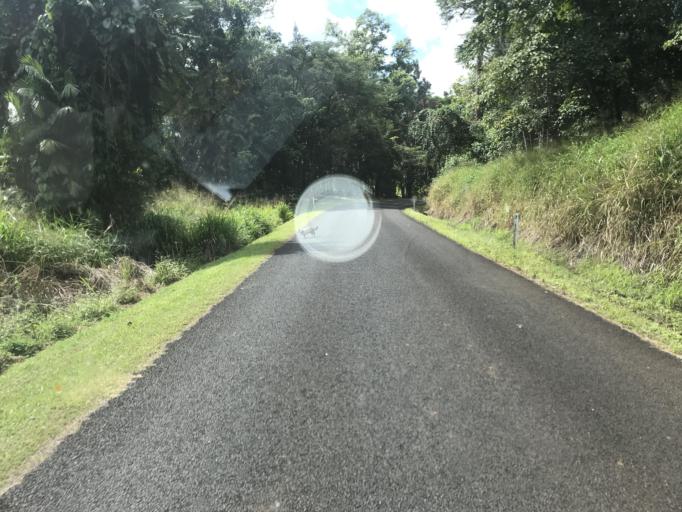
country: AU
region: Queensland
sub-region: Cassowary Coast
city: Innisfail
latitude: -17.5502
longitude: 145.8680
